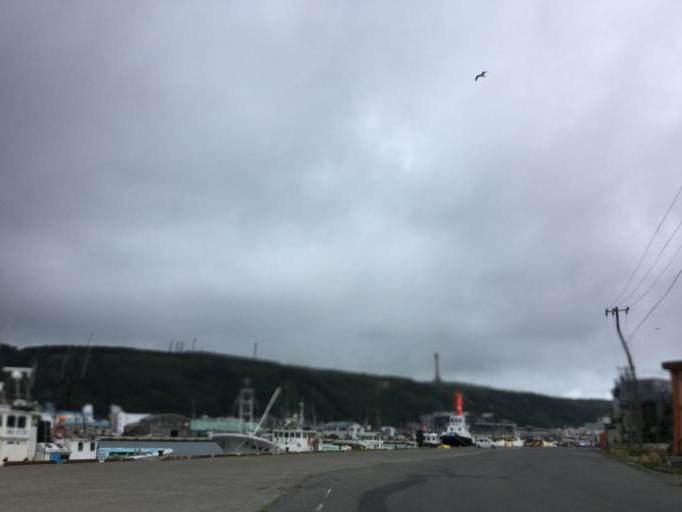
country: JP
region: Hokkaido
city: Wakkanai
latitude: 45.4053
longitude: 141.6805
